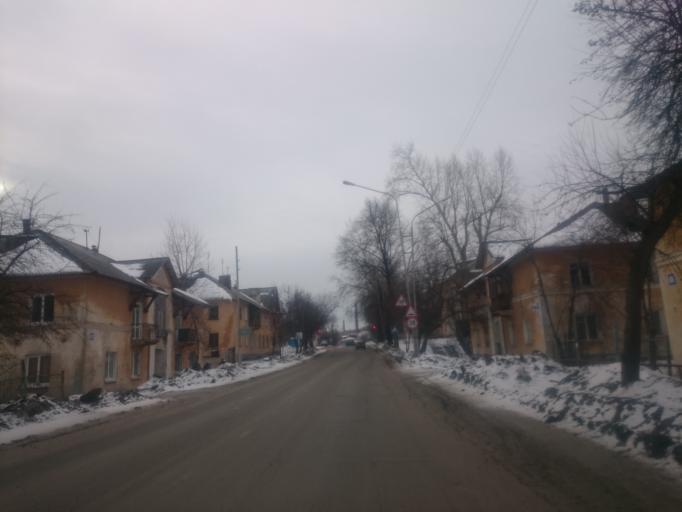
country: RU
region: Sverdlovsk
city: Irbit
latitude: 57.6704
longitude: 63.0590
